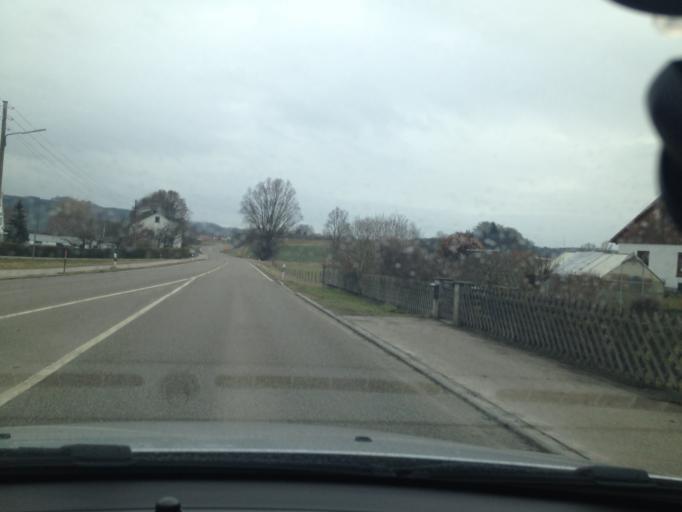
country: DE
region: Bavaria
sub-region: Swabia
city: Altenmunster
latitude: 48.4450
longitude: 10.5885
